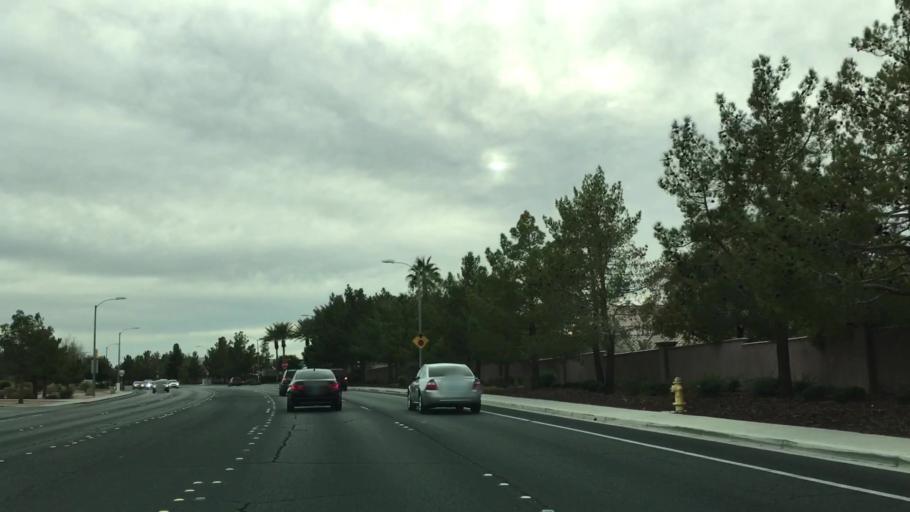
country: US
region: Nevada
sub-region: Clark County
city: Whitney
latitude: 36.0136
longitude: -115.0941
